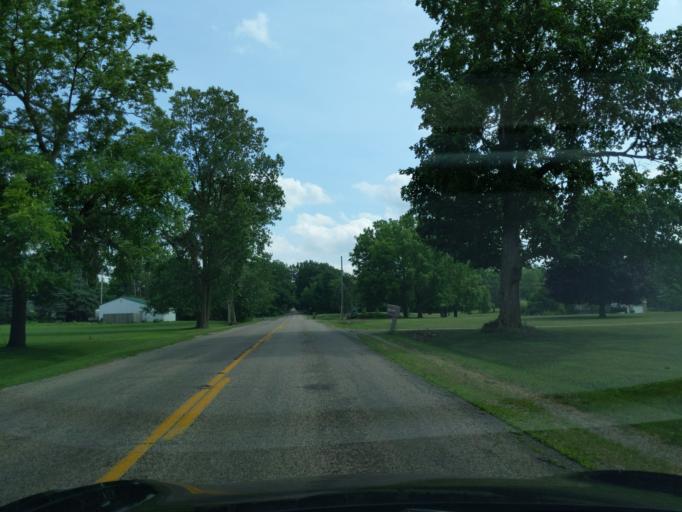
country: US
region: Michigan
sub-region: Eaton County
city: Eaton Rapids
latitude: 42.5692
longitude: -84.6021
